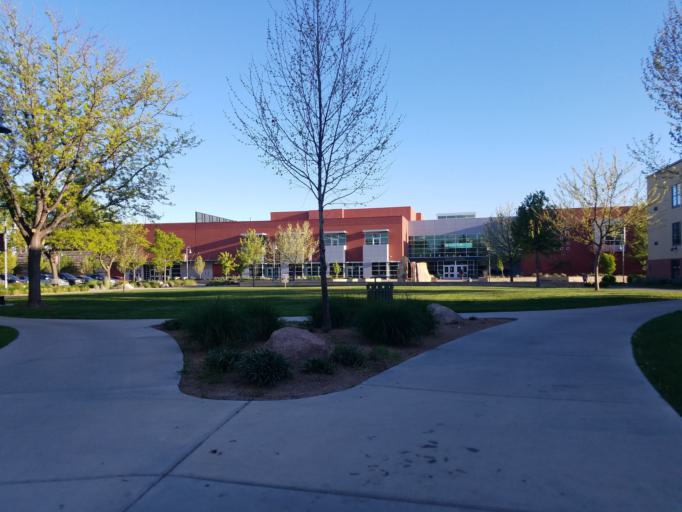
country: US
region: Colorado
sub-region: Mesa County
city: Grand Junction
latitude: 39.0817
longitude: -108.5535
